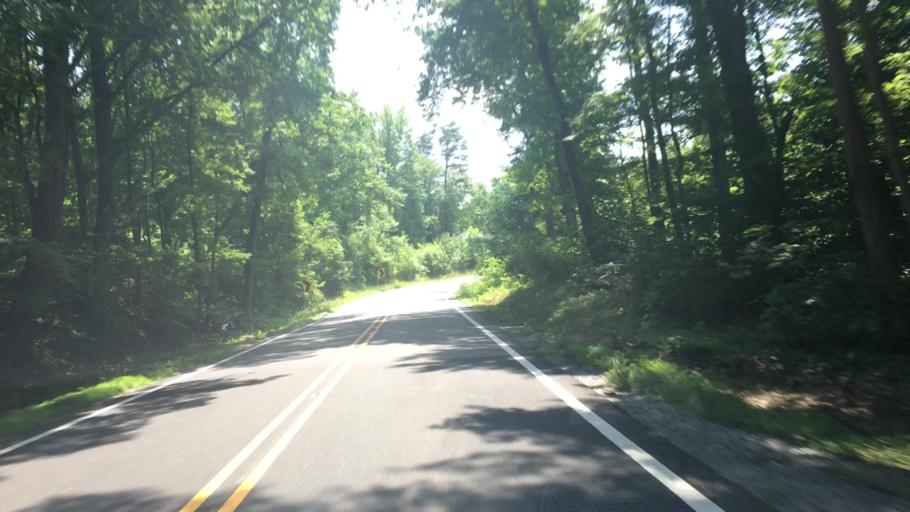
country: US
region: Virginia
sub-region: King George County
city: King George
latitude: 38.3198
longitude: -77.1870
